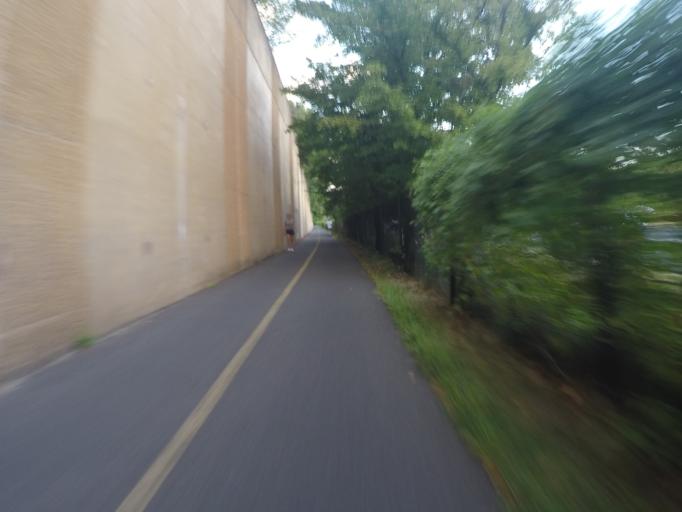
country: US
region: Virginia
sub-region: Arlington County
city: Arlington
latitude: 38.8931
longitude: -77.1012
